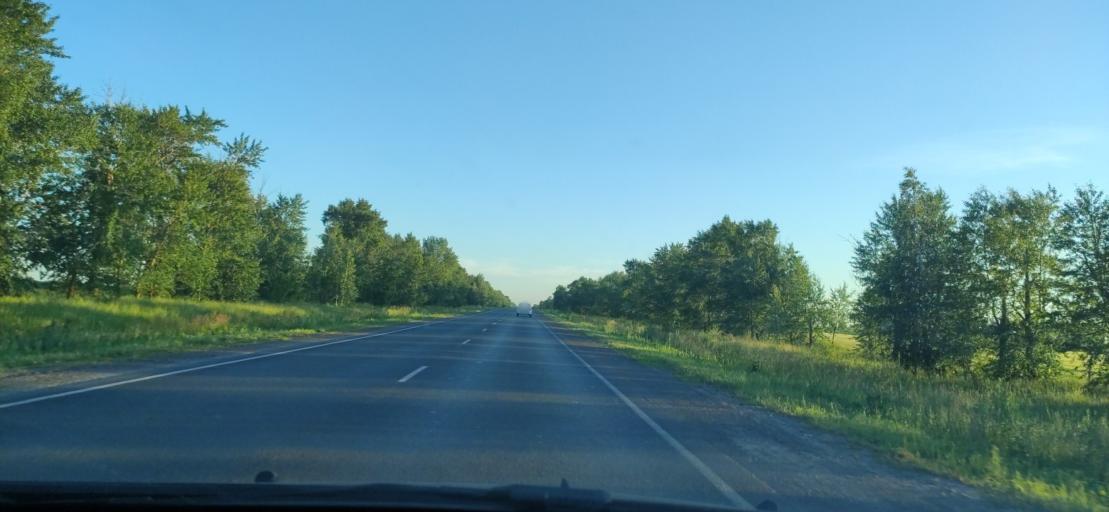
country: RU
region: Ulyanovsk
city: Cherdakly
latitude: 54.4106
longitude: 48.8779
